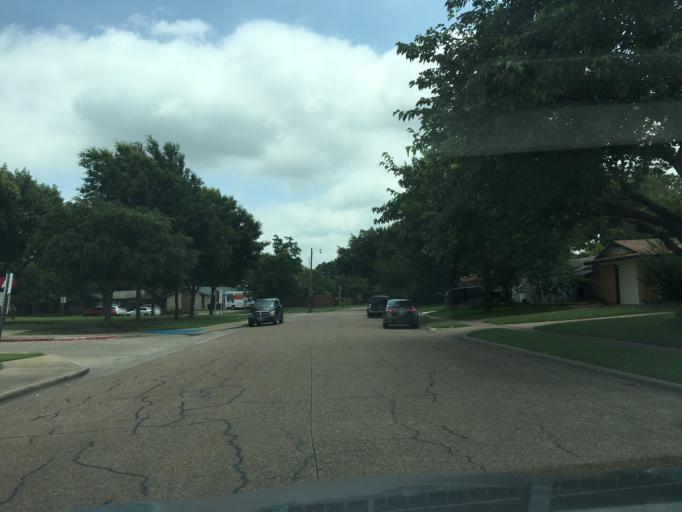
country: US
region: Texas
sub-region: Dallas County
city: Garland
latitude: 32.9215
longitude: -96.6780
